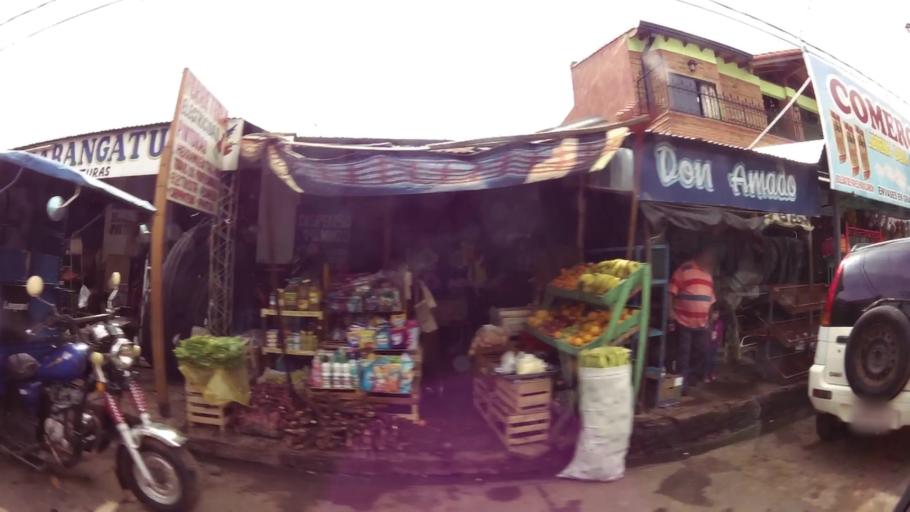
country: PY
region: Central
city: Limpio
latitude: -25.1703
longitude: -57.4743
